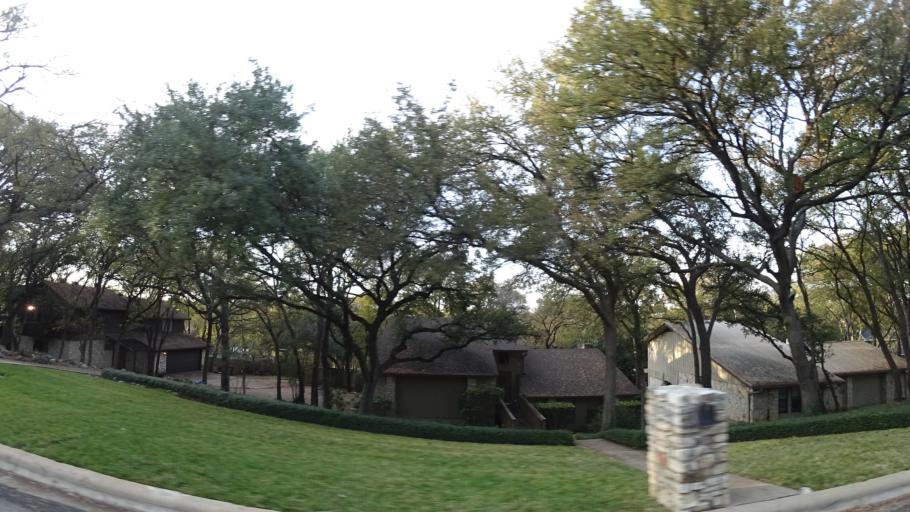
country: US
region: Texas
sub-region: Williamson County
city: Round Rock
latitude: 30.5067
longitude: -97.6707
